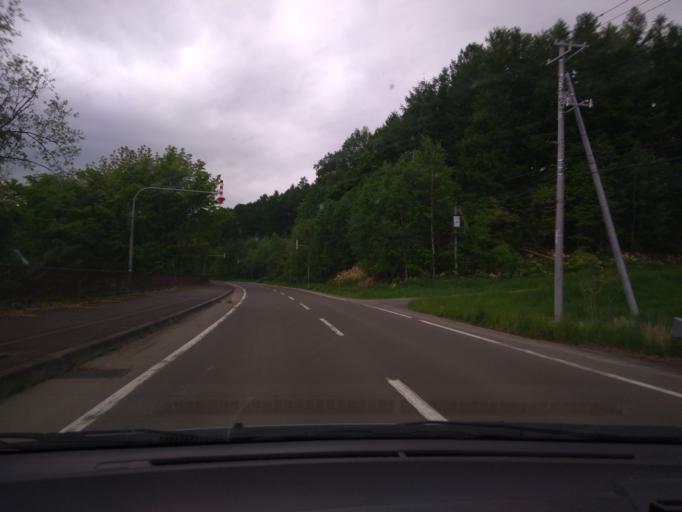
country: JP
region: Hokkaido
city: Shimo-furano
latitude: 43.1743
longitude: 142.5601
